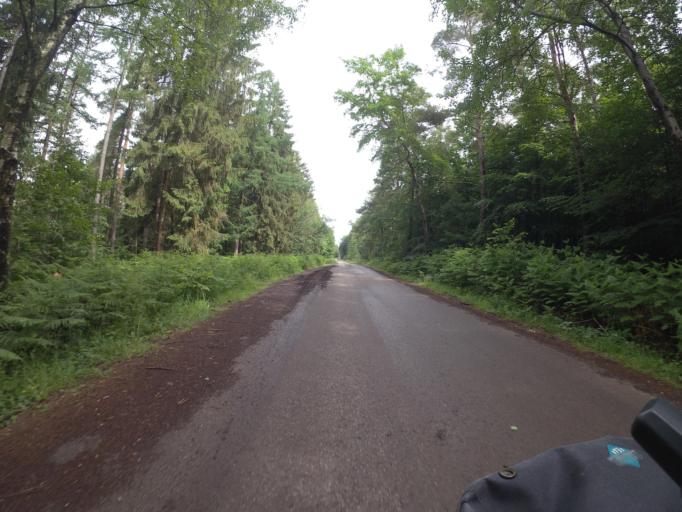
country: DE
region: North Rhine-Westphalia
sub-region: Regierungsbezirk Koln
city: Hurtgenwald
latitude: 50.7439
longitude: 6.3854
